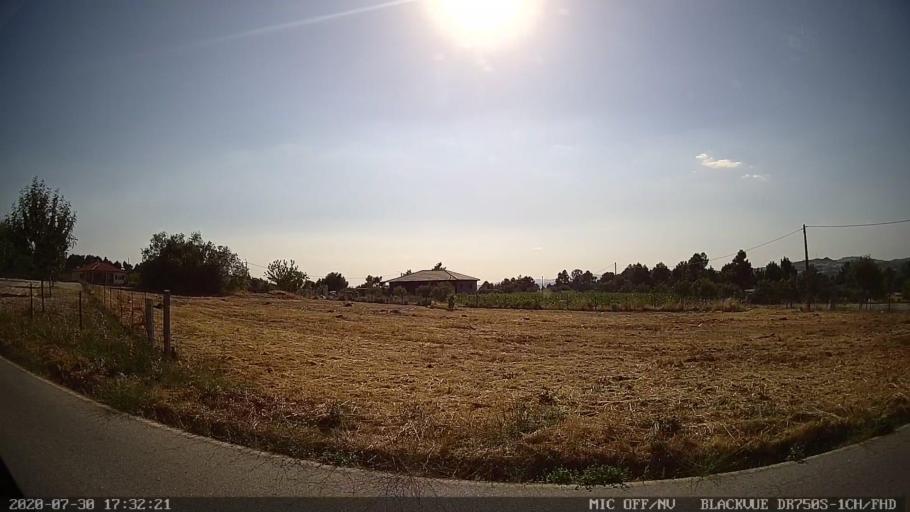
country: PT
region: Vila Real
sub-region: Murca
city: Murca
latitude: 41.3485
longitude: -7.4737
